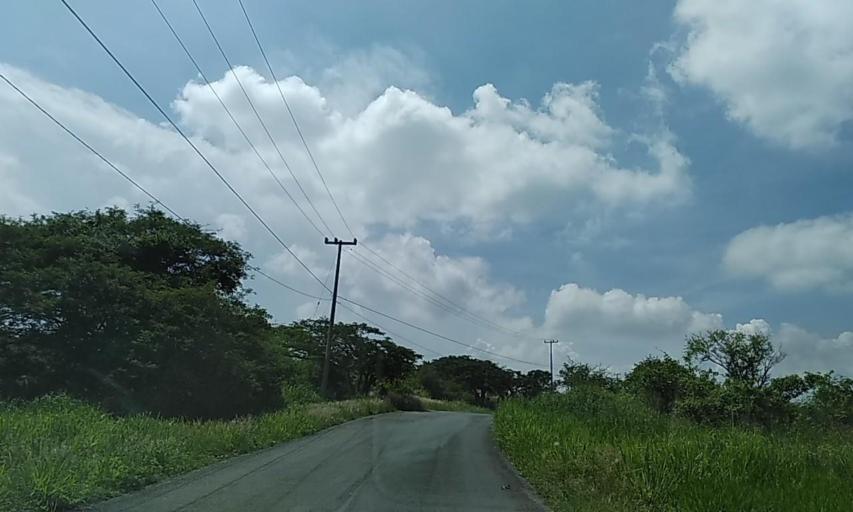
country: MX
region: Veracruz
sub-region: Emiliano Zapata
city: Dos Rios
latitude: 19.4396
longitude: -96.7801
